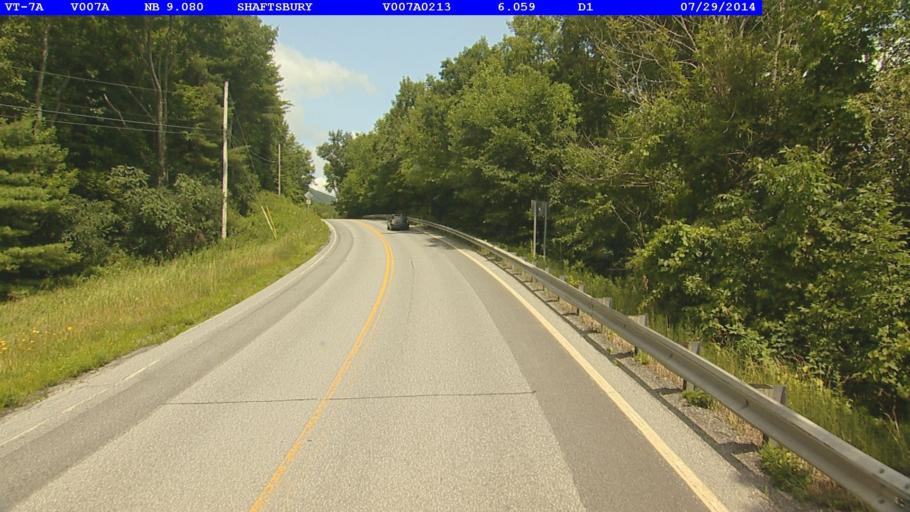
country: US
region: Vermont
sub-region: Bennington County
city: Arlington
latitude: 43.0163
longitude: -73.1908
